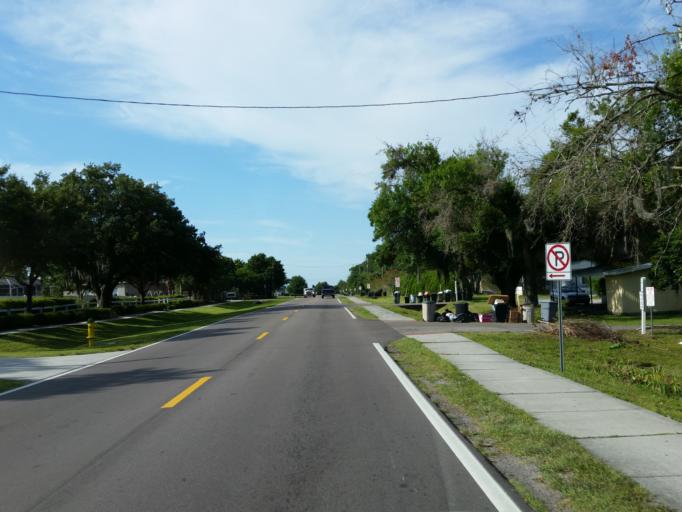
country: US
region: Florida
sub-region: Hillsborough County
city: Gibsonton
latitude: 27.8418
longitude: -82.3517
